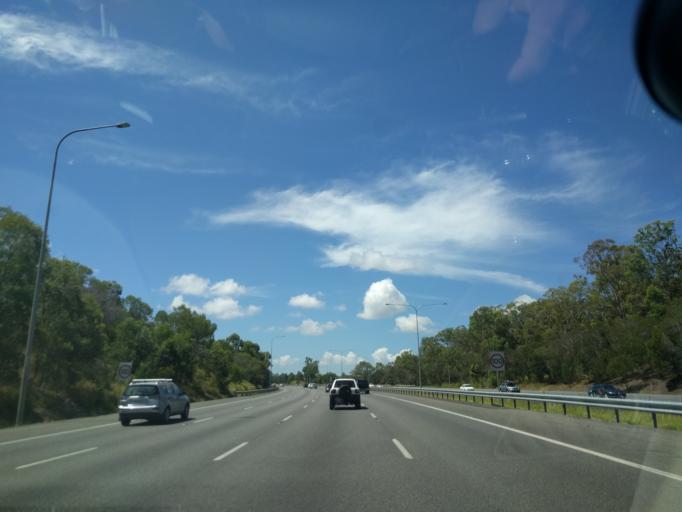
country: AU
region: Queensland
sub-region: Moreton Bay
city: Murrumba Downs
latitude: -27.2879
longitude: 153.0200
